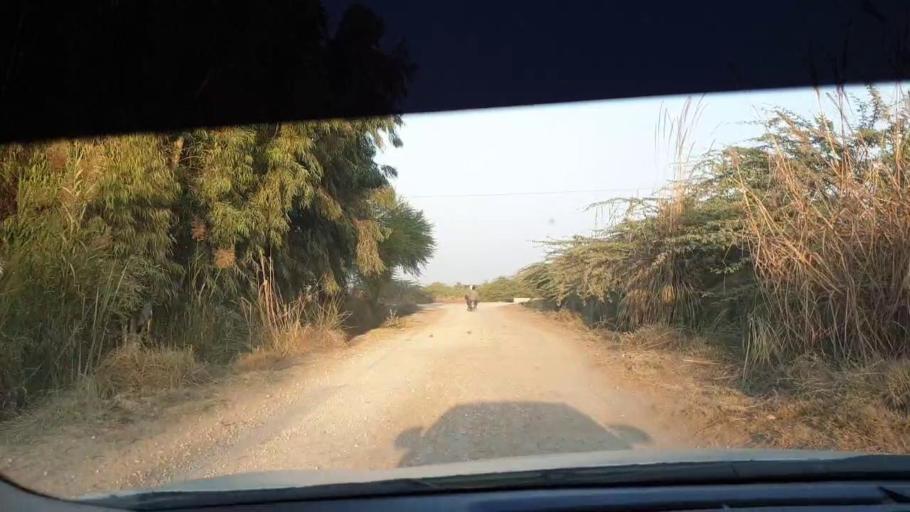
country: PK
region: Sindh
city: Berani
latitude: 25.8632
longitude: 68.8258
